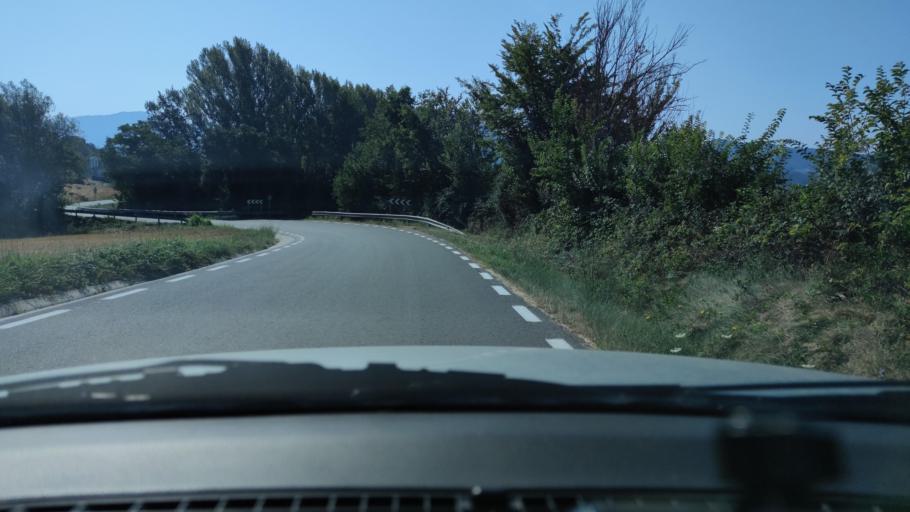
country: ES
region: Catalonia
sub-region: Provincia de Lleida
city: Tremp
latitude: 42.2123
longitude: 0.9385
